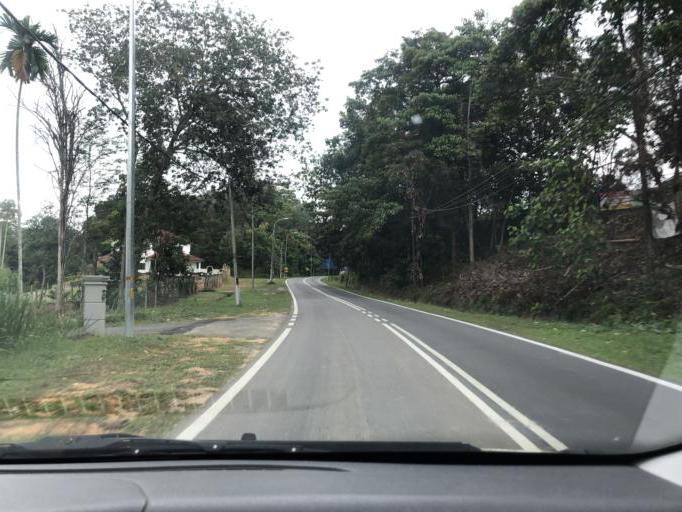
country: MY
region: Putrajaya
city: Putrajaya
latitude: 2.9201
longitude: 101.7490
